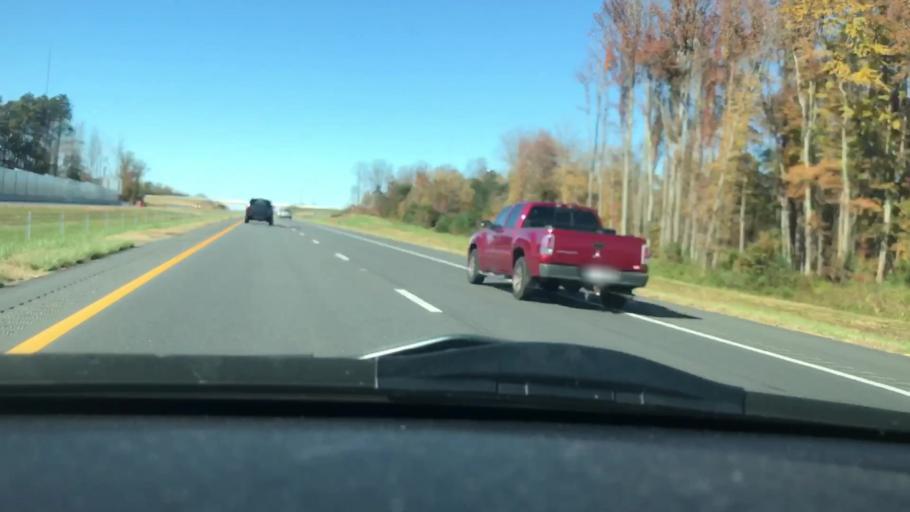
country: US
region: North Carolina
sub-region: Guilford County
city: Summerfield
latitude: 36.2615
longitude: -79.9270
